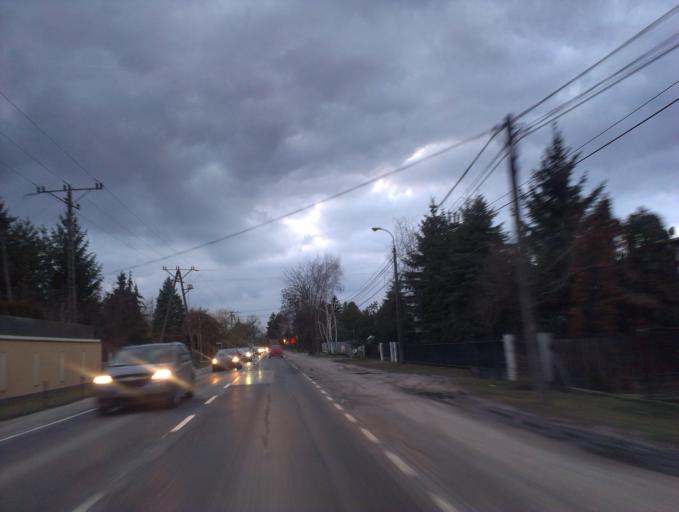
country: PL
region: Masovian Voivodeship
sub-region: Powiat piaseczynski
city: Jozefoslaw
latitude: 52.0851
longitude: 21.0733
